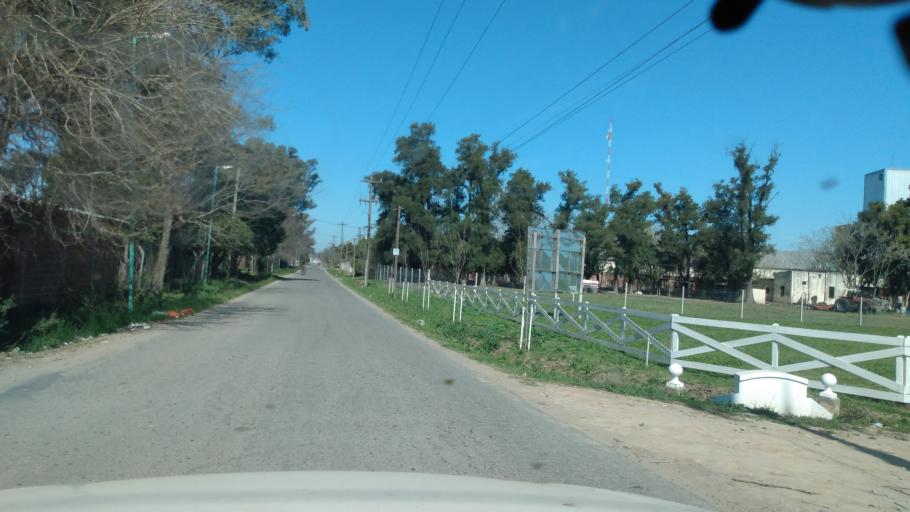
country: AR
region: Buenos Aires
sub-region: Partido de Lujan
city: Lujan
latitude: -34.5829
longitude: -59.1199
